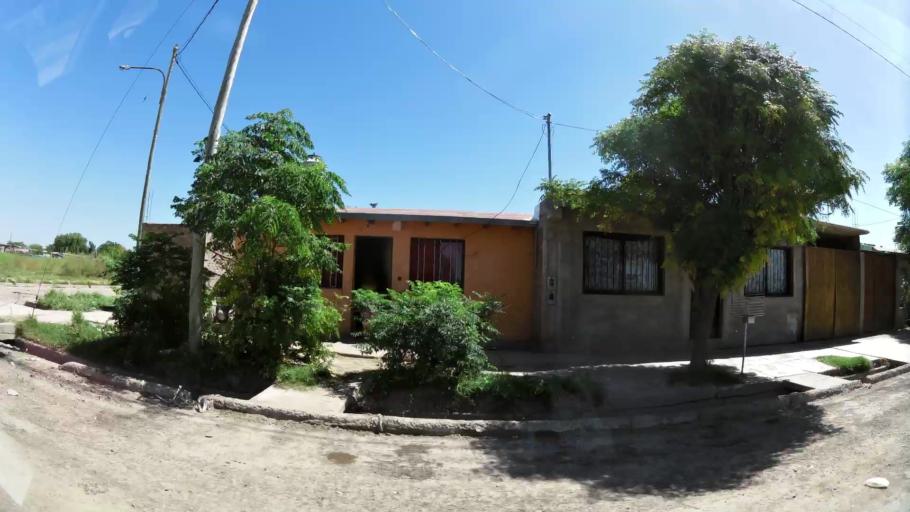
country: AR
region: Mendoza
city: Villa Nueva
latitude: -32.8744
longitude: -68.7846
